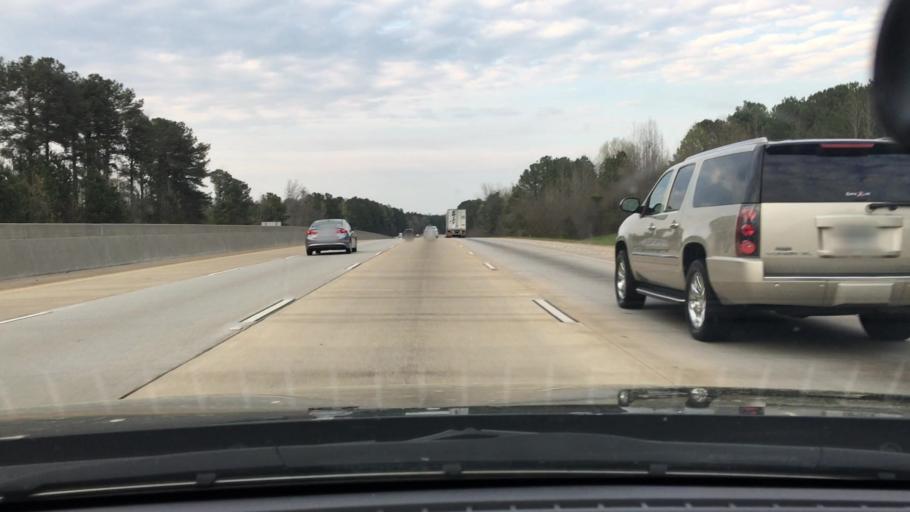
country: US
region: Georgia
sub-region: Coweta County
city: Newnan
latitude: 33.4188
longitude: -84.7298
